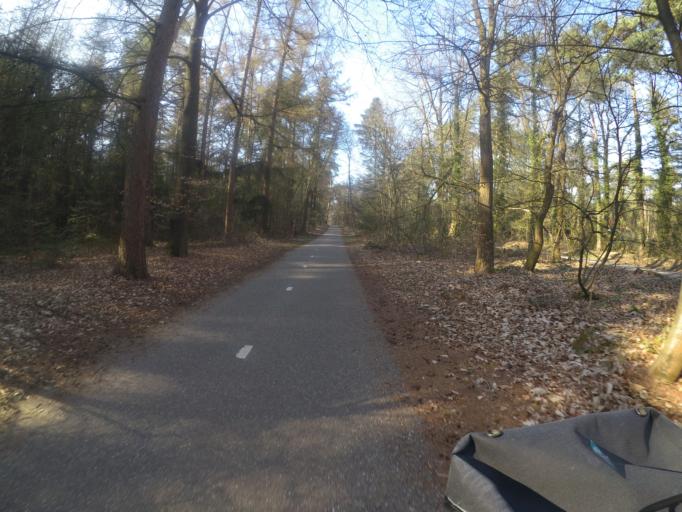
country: NL
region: North Brabant
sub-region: Gemeente Oisterwijk
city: Oisterwijk
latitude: 51.5651
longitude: 5.2194
